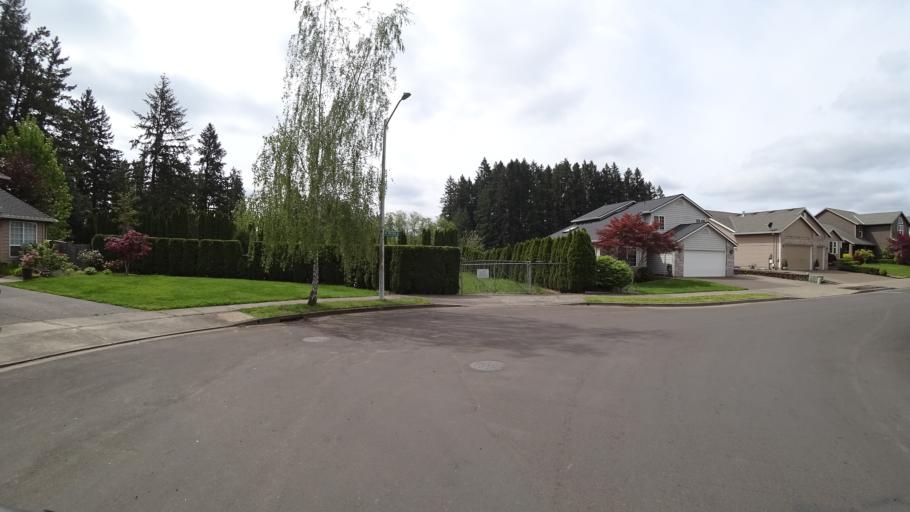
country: US
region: Oregon
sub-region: Washington County
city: Hillsboro
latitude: 45.5439
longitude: -122.9901
